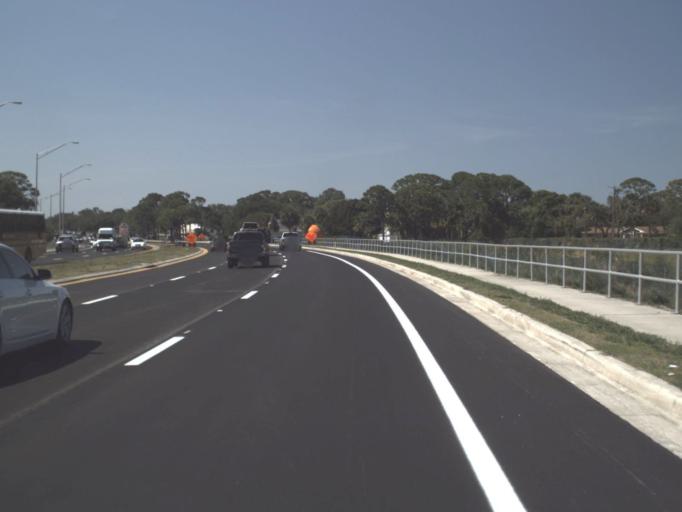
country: US
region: Florida
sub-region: Brevard County
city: Indian Harbour Beach
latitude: 28.1419
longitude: -80.6342
